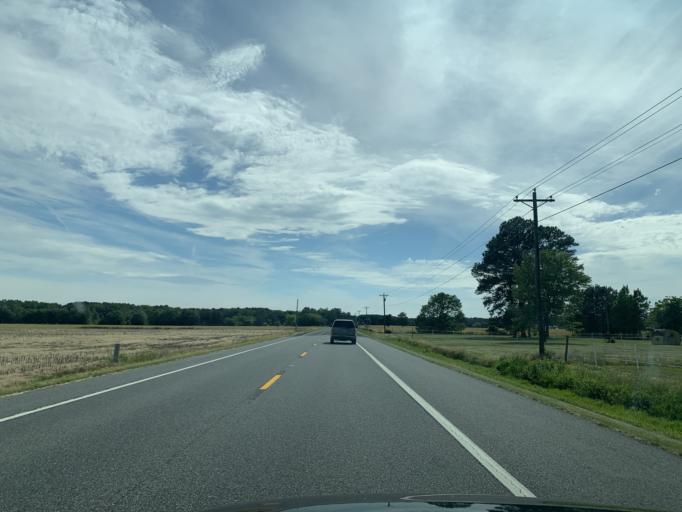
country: US
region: Maryland
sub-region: Worcester County
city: Berlin
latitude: 38.3086
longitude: -75.3142
